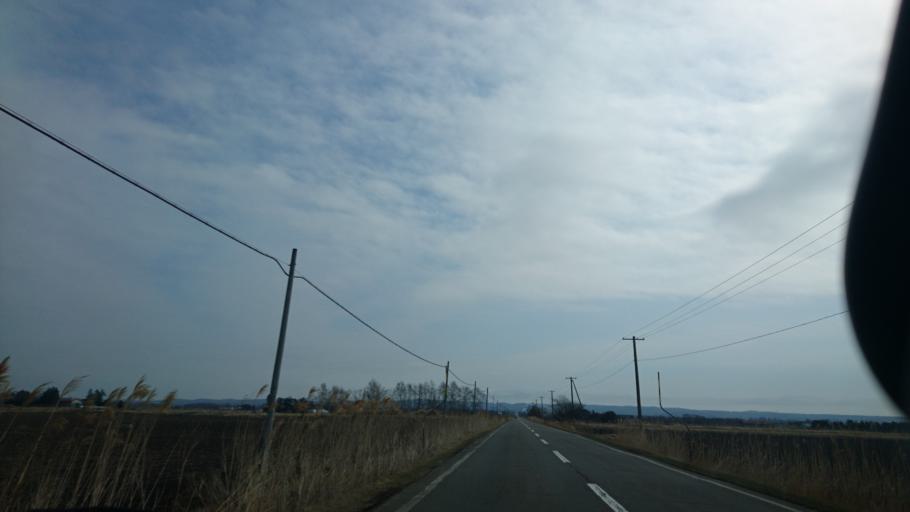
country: JP
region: Hokkaido
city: Otofuke
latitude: 43.0389
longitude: 143.2219
